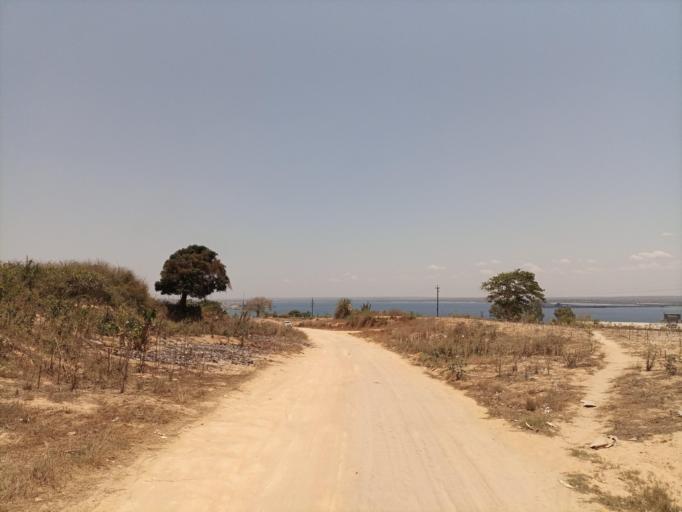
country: MZ
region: Nampula
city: Nacala
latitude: -14.5187
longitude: 40.6805
